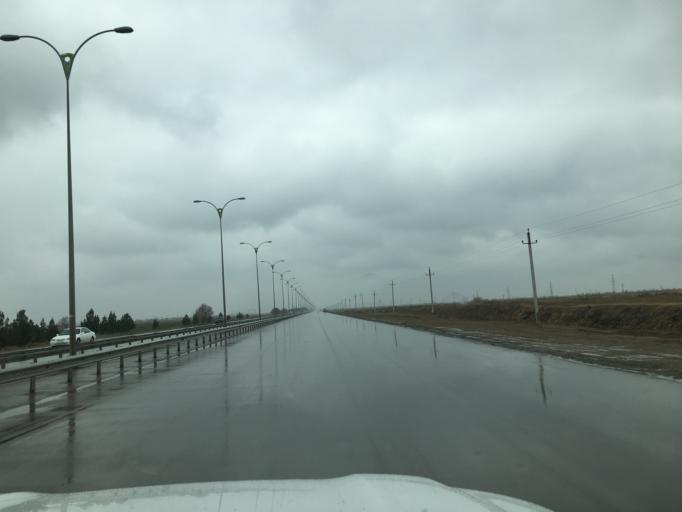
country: TM
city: Murgab
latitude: 37.5108
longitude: 61.9373
